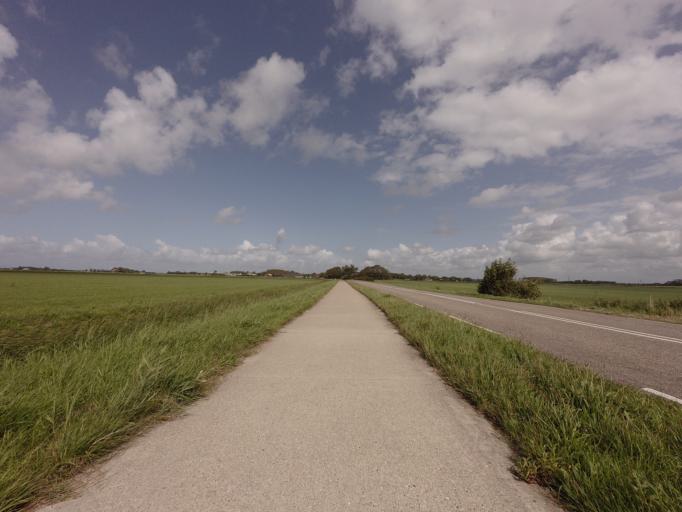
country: NL
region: Friesland
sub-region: Gemeente Harlingen
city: Harlingen
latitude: 53.1414
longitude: 5.4763
